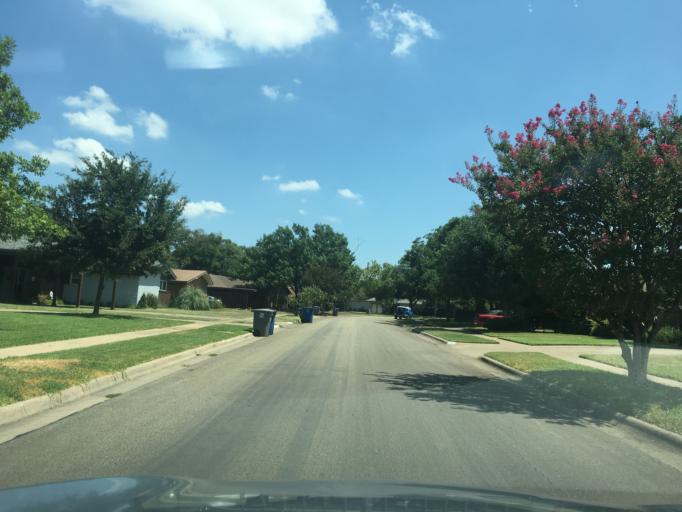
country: US
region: Texas
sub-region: Dallas County
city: Garland
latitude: 32.8682
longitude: -96.6931
